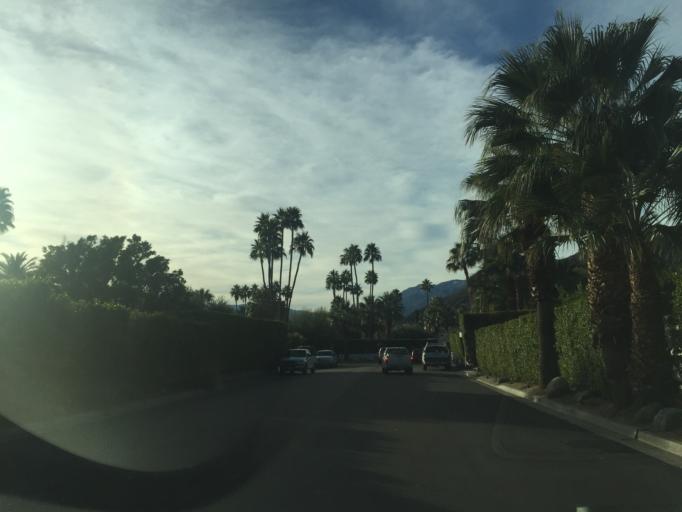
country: US
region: California
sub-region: Riverside County
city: Palm Springs
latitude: 33.8429
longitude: -116.5520
